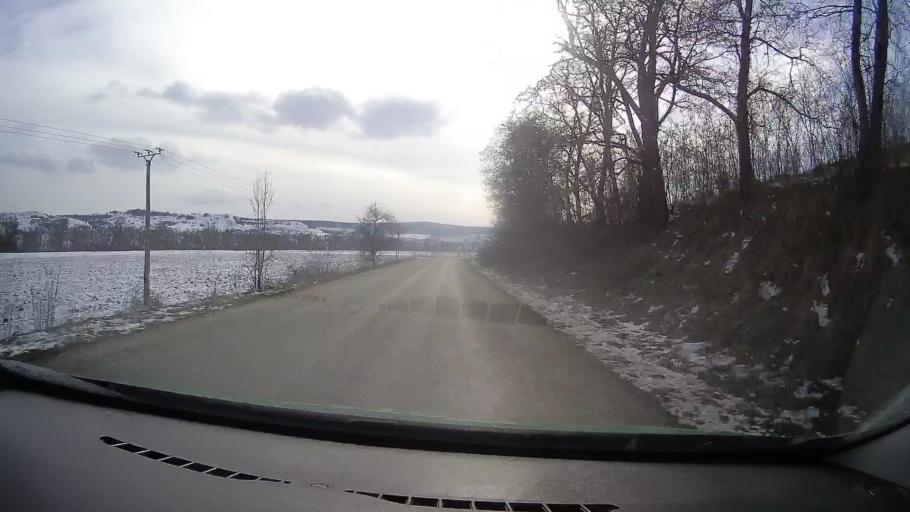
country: RO
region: Sibiu
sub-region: Comuna Iacobeni
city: Iacobeni
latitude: 46.0471
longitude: 24.7632
